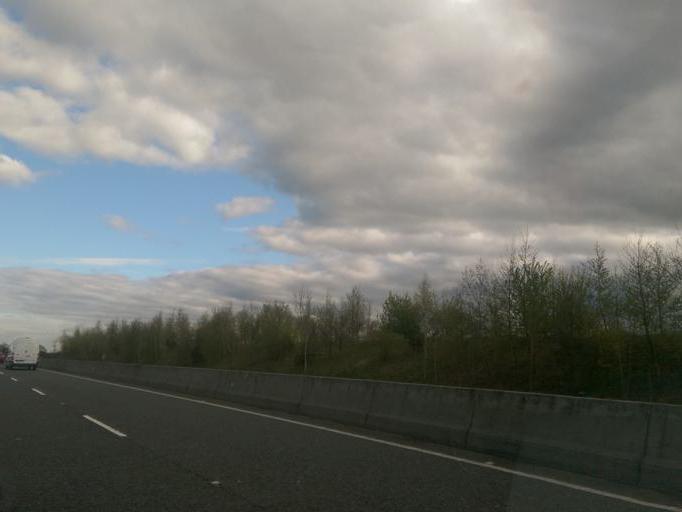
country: IE
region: Leinster
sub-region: An Iarmhi
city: Kilbeggan
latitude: 53.3769
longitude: -7.5574
